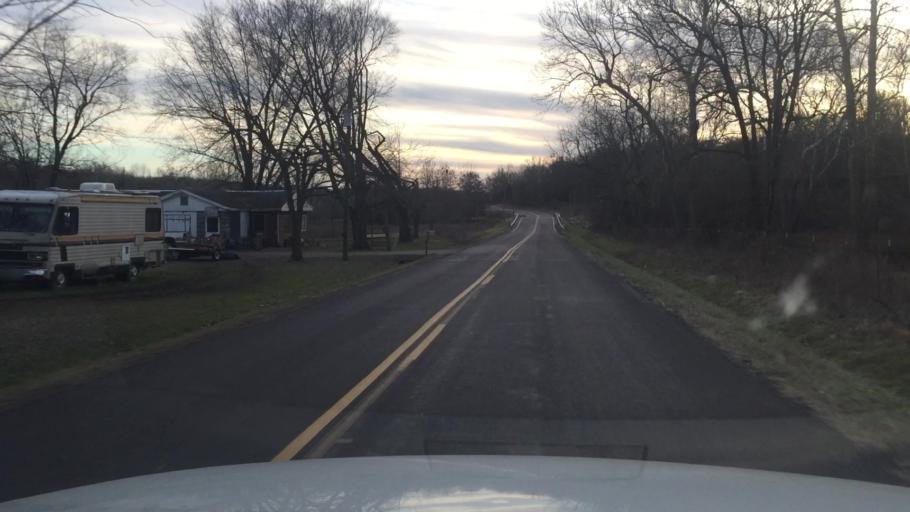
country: US
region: Missouri
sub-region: Miller County
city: Eldon
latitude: 38.3637
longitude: -92.6850
